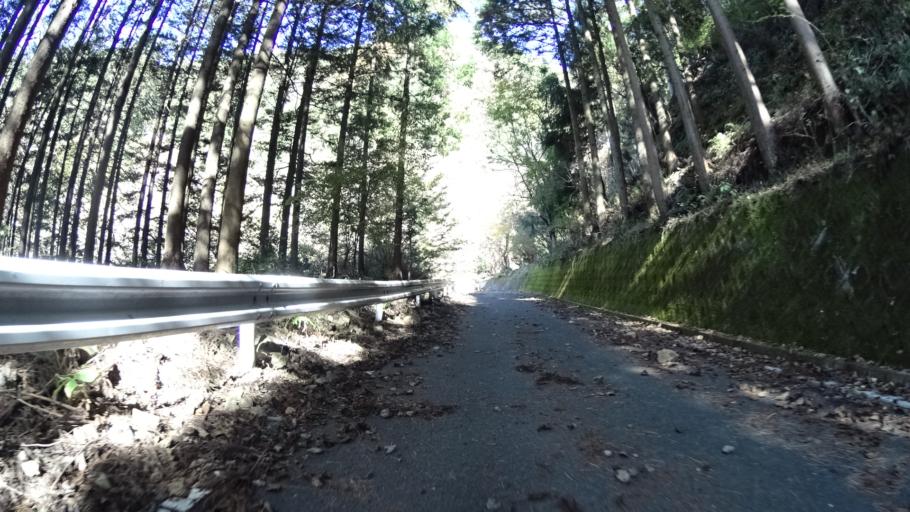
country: JP
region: Kanagawa
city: Atsugi
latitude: 35.5037
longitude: 139.2757
